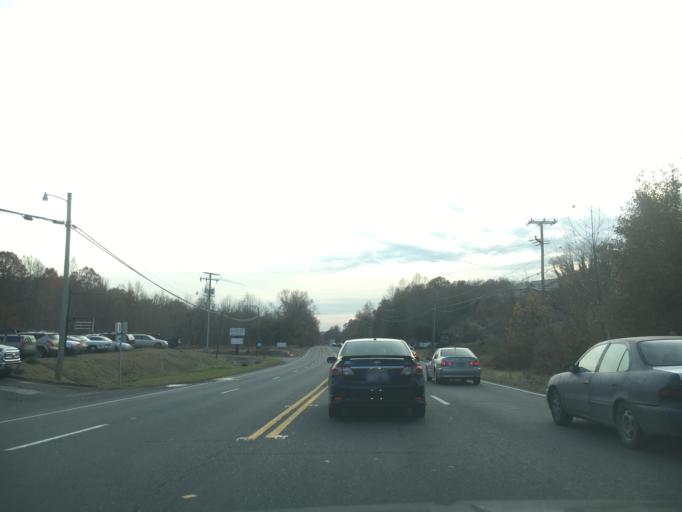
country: US
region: Virginia
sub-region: Stafford County
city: Aquia Harbour
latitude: 38.4921
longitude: -77.3808
